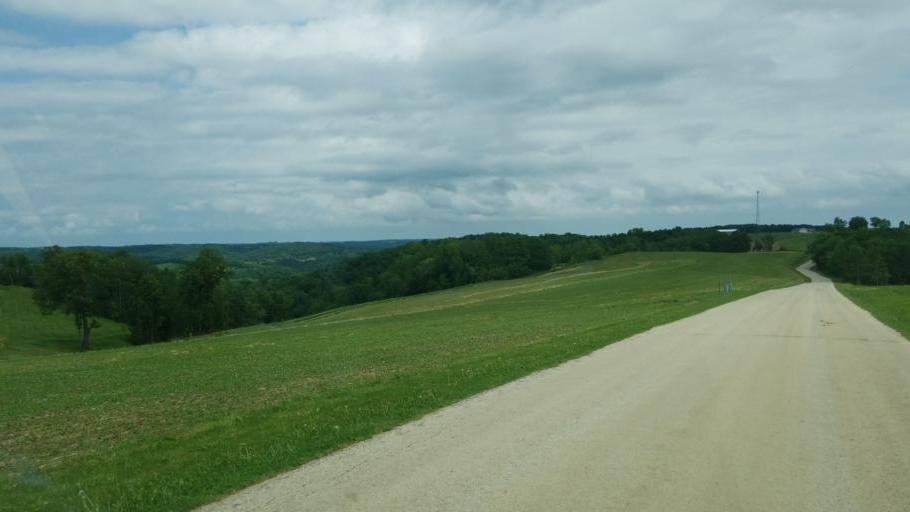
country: US
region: Wisconsin
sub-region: Monroe County
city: Cashton
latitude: 43.7058
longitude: -90.6212
